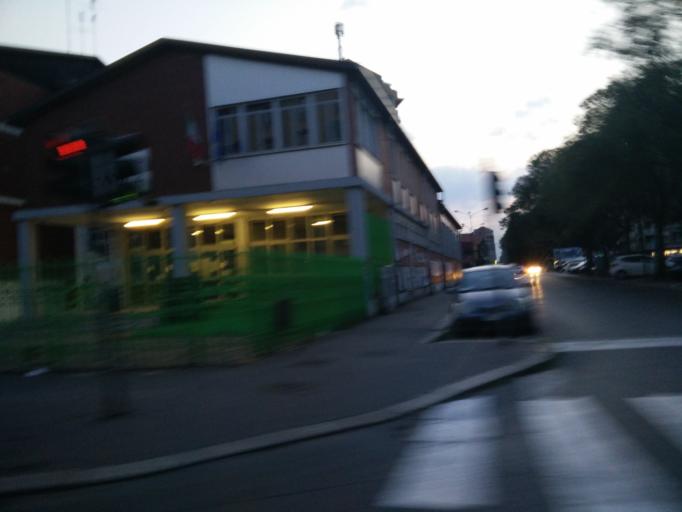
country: IT
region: Piedmont
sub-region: Provincia di Torino
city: Lesna
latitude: 45.0448
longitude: 7.6455
